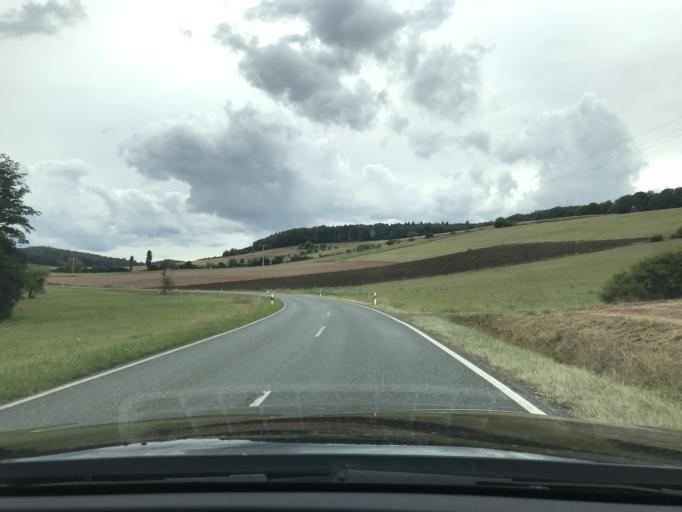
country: DE
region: Bavaria
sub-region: Regierungsbezirk Unterfranken
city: Burgpreppach
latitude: 50.1050
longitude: 10.6767
